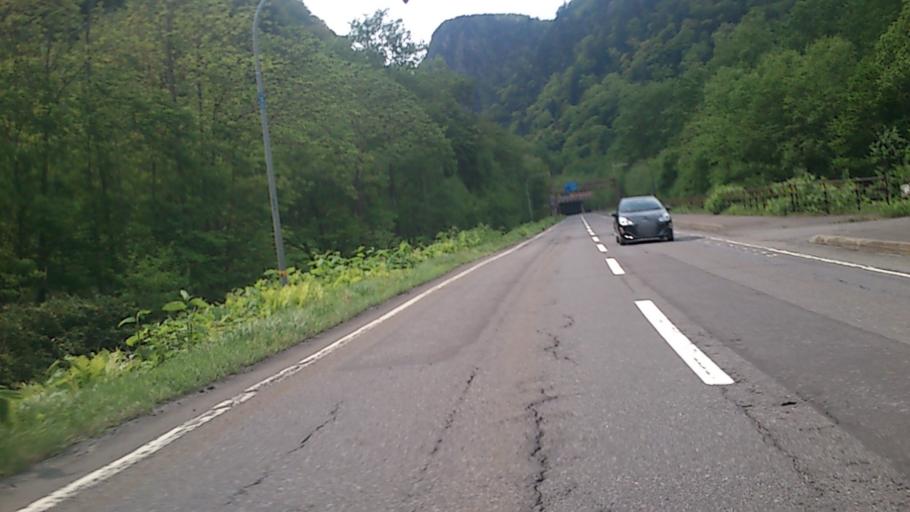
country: JP
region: Hokkaido
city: Kamikawa
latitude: 43.7474
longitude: 142.9344
